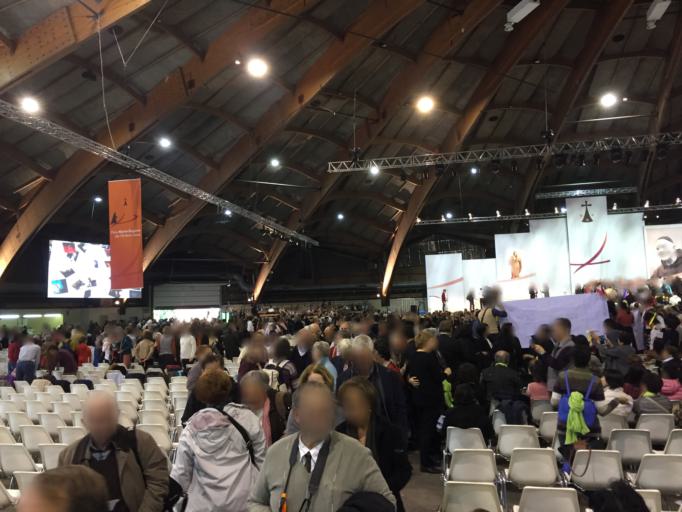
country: FR
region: Provence-Alpes-Cote d'Azur
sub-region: Departement des Bouches-du-Rhone
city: Noves
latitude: 43.9068
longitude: 4.8911
